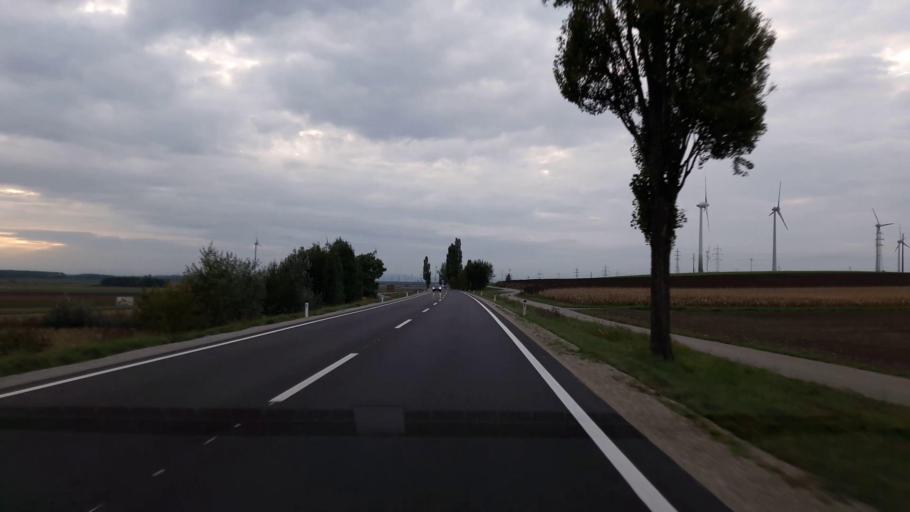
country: AT
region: Lower Austria
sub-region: Politischer Bezirk Bruck an der Leitha
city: Bruck an der Leitha
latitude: 48.0271
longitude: 16.7349
